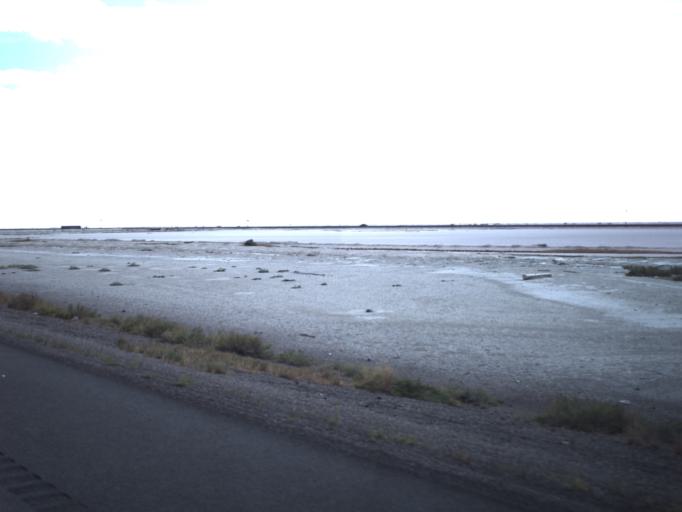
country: US
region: Utah
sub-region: Tooele County
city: Wendover
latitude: 40.7408
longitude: -113.9547
